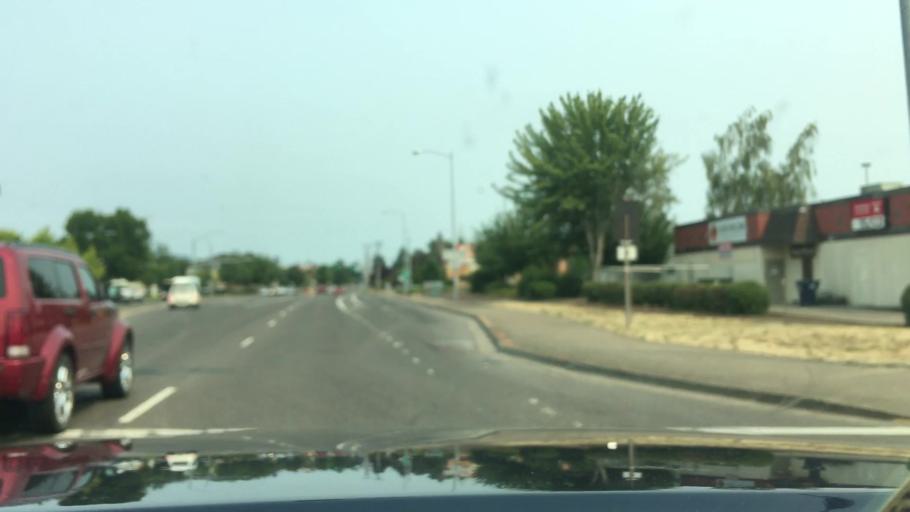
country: US
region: Oregon
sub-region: Lane County
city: Eugene
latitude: 44.0845
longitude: -123.1705
